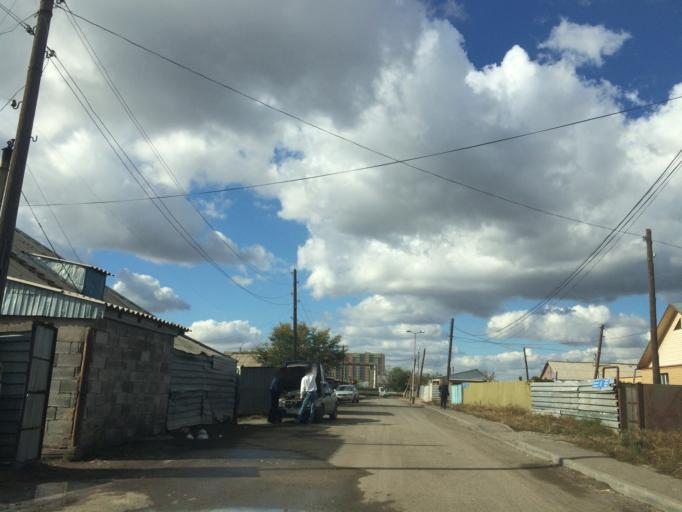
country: KZ
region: Astana Qalasy
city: Astana
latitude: 51.1861
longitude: 71.3917
